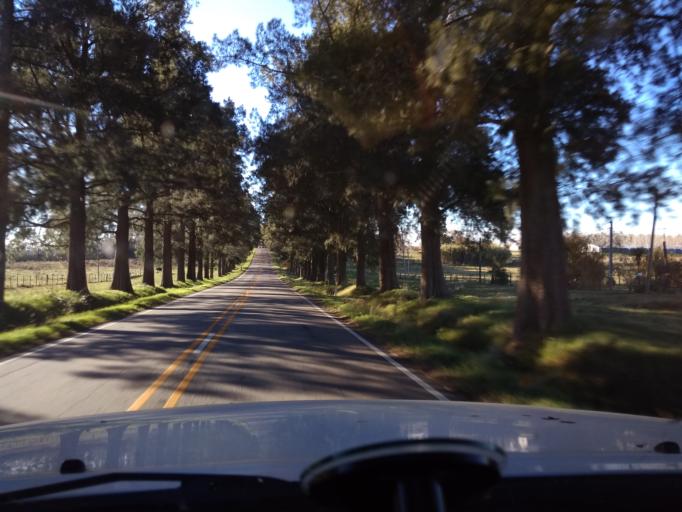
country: UY
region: Canelones
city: San Ramon
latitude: -34.3621
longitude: -55.9594
